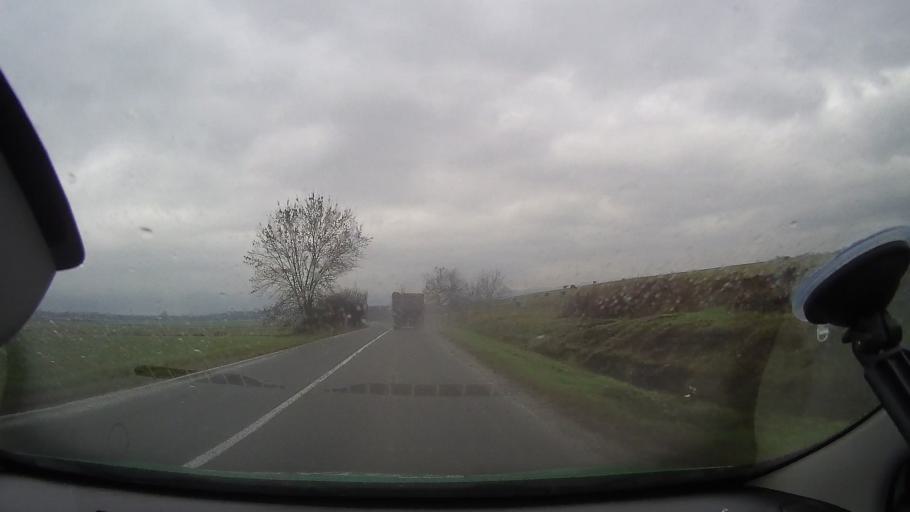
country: RO
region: Arad
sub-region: Comuna Dieci
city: Dieci
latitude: 46.2794
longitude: 22.2883
